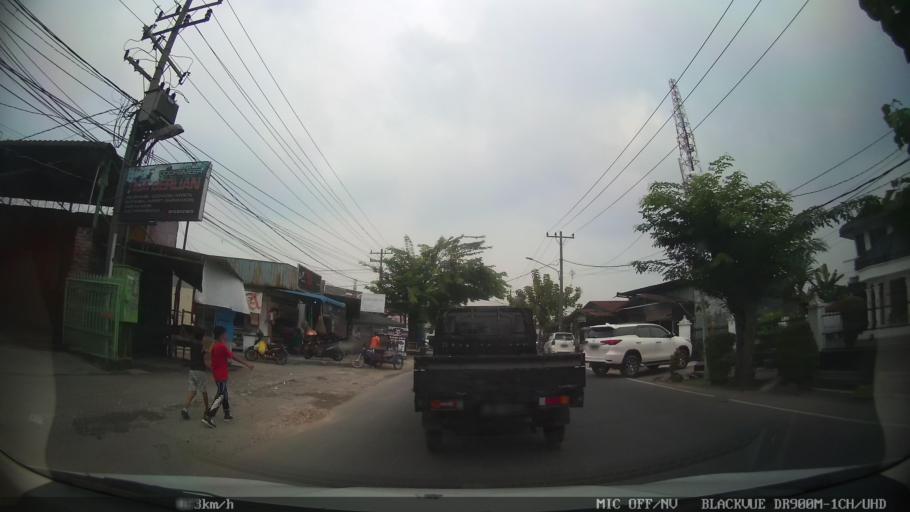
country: ID
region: North Sumatra
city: Medan
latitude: 3.5576
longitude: 98.7184
